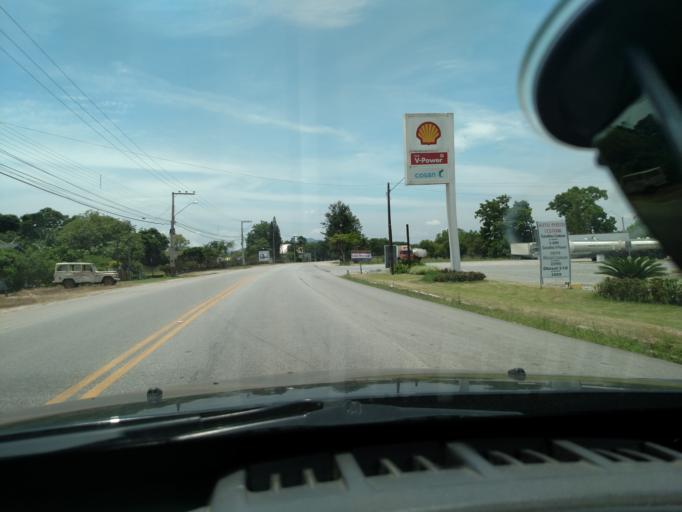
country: BR
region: Santa Catarina
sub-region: Gaspar
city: Gaspar
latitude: -26.9116
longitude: -48.9179
